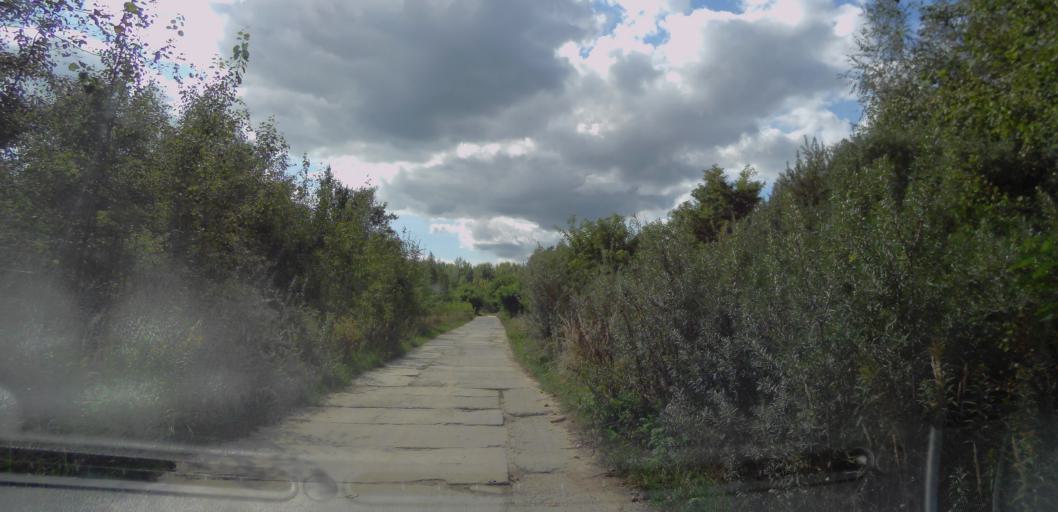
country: PL
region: Subcarpathian Voivodeship
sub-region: Tarnobrzeg
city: Tarnobrzeg
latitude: 50.5339
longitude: 21.6632
